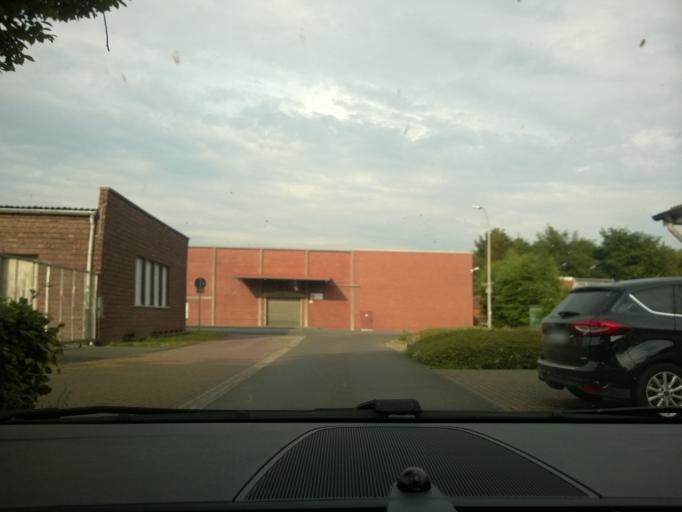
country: DE
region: North Rhine-Westphalia
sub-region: Regierungsbezirk Munster
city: Gescher
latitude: 51.9533
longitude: 7.0131
